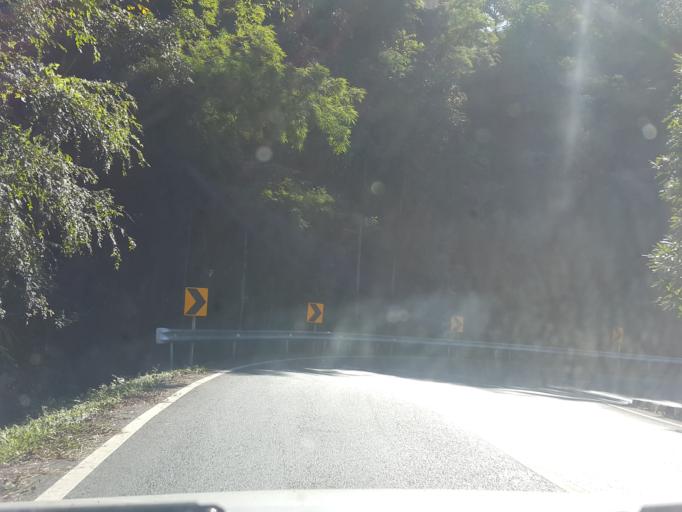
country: TH
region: Mae Hong Son
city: Mae Hi
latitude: 19.2649
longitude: 98.5076
